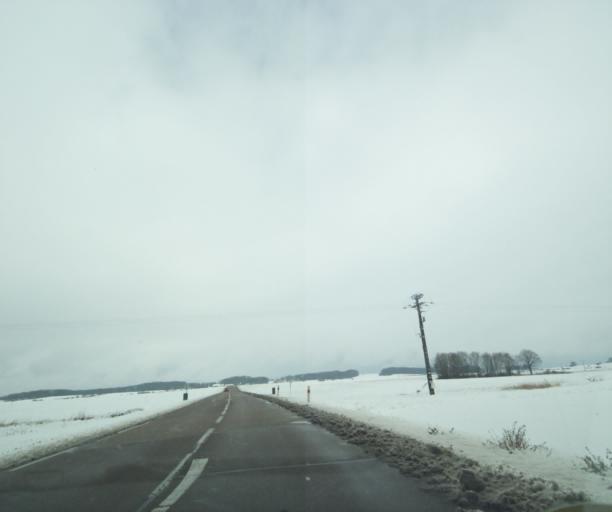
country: FR
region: Champagne-Ardenne
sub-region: Departement de la Haute-Marne
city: Montier-en-Der
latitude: 48.4372
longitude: 4.7290
